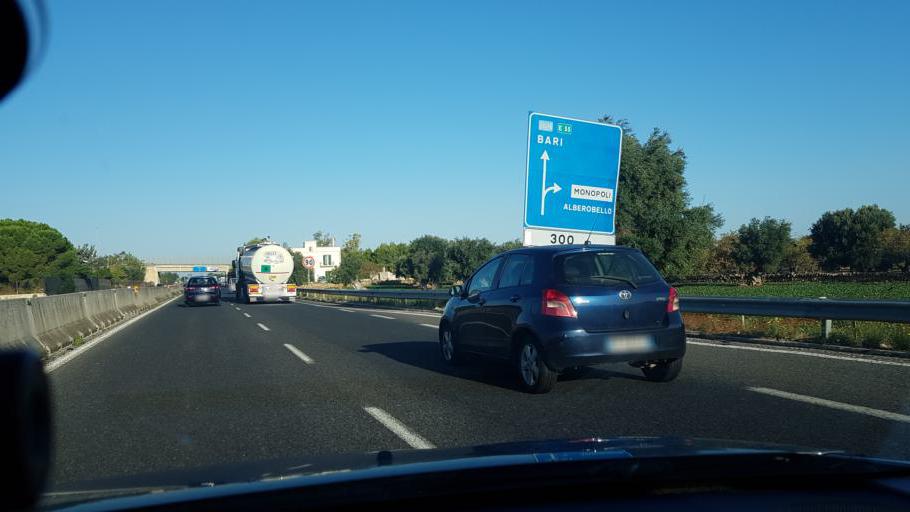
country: IT
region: Apulia
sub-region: Provincia di Bari
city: Monopoli
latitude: 40.9344
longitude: 17.2947
